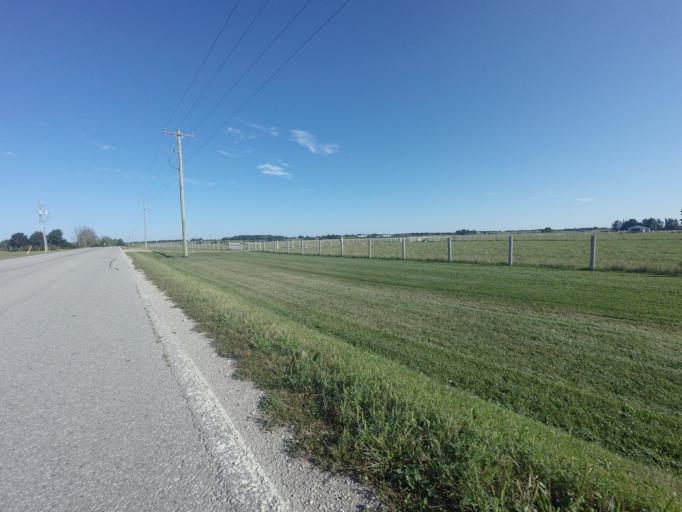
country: CA
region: Ontario
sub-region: Wellington County
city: Guelph
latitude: 43.6471
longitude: -80.4109
